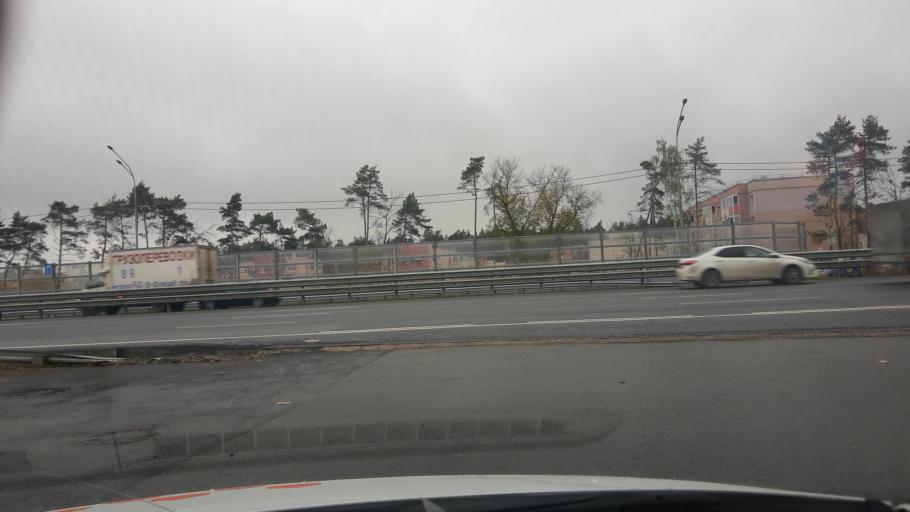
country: RU
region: Moskovskaya
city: Chornaya
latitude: 55.8072
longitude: 38.0596
